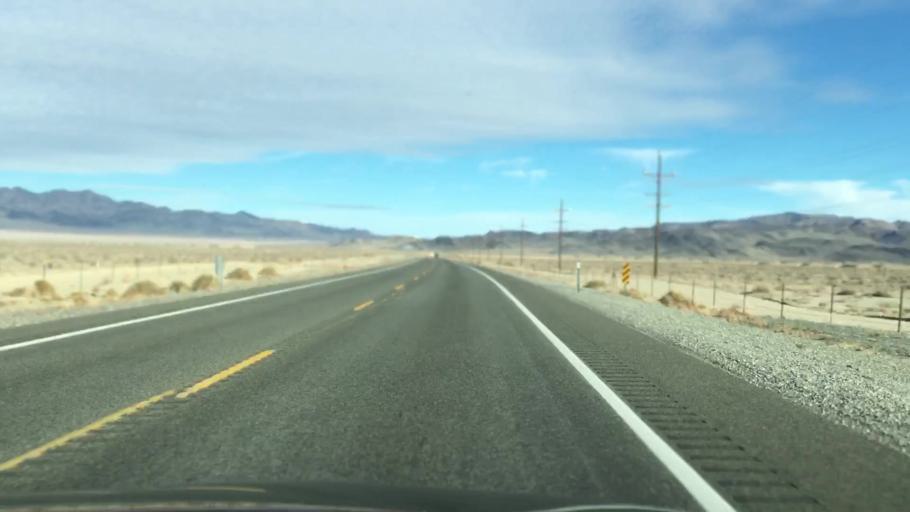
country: US
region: Nevada
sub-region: Mineral County
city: Hawthorne
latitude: 38.5251
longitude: -118.5751
